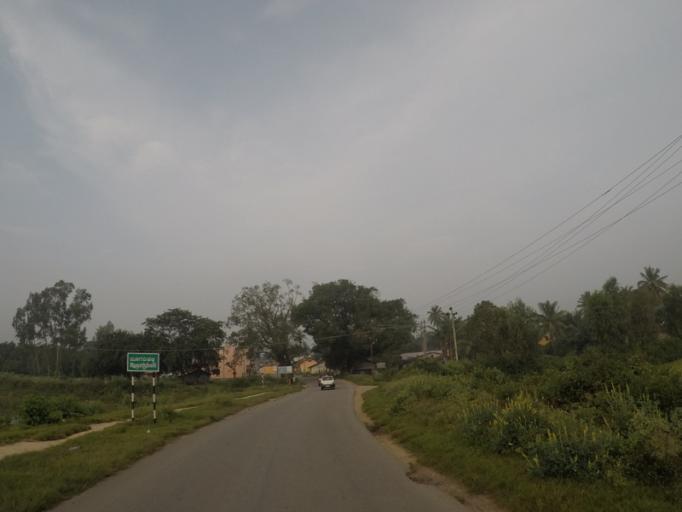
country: IN
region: Karnataka
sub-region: Chikmagalur
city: Chikmagalur
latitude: 13.2861
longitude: 75.7488
